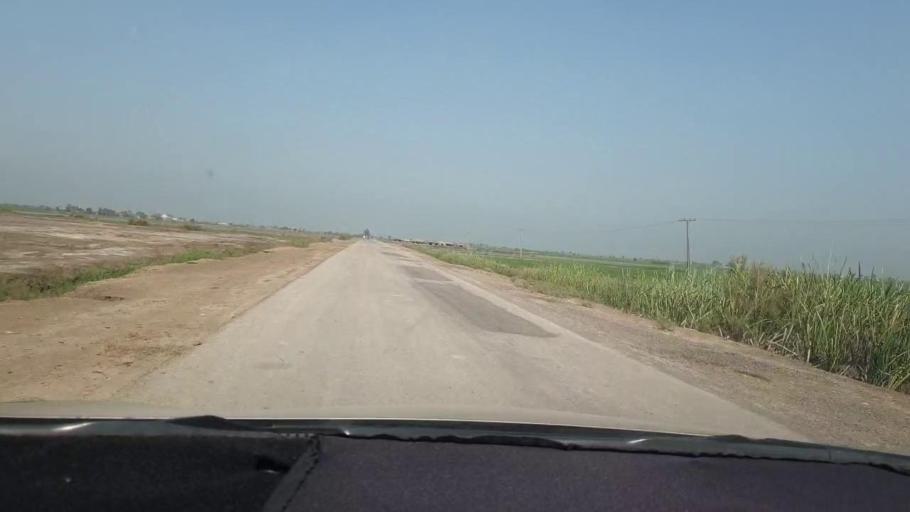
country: PK
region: Sindh
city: Miro Khan
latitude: 27.8318
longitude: 68.0142
